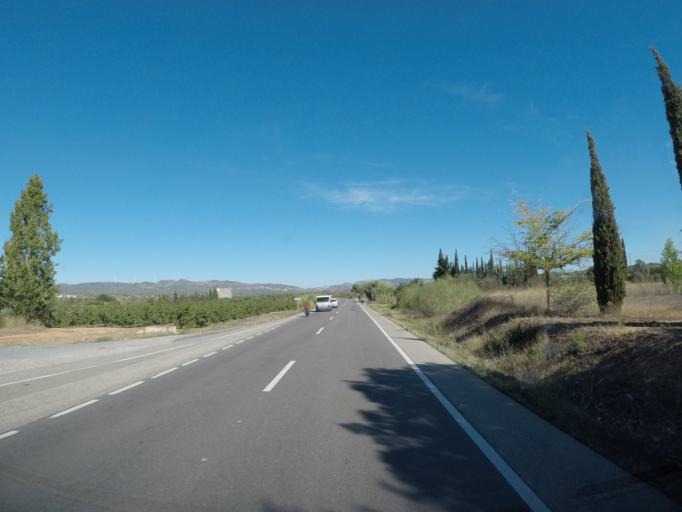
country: ES
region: Catalonia
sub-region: Provincia de Tarragona
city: Ginestar
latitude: 41.0801
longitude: 0.6614
